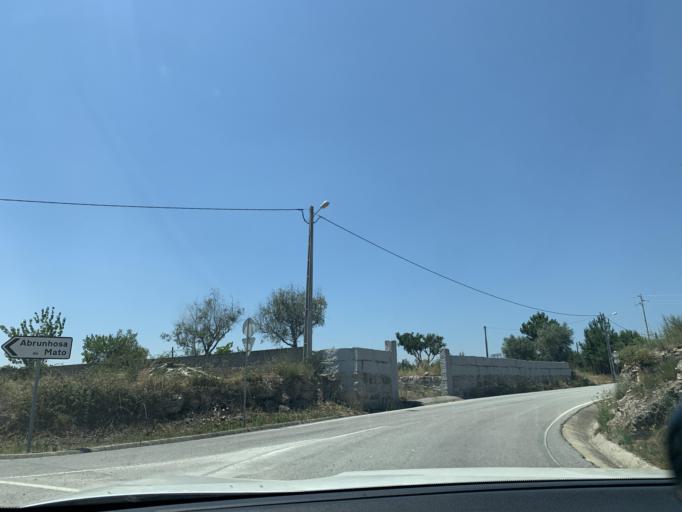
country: PT
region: Viseu
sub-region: Mangualde
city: Mangualde
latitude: 40.5478
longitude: -7.7407
